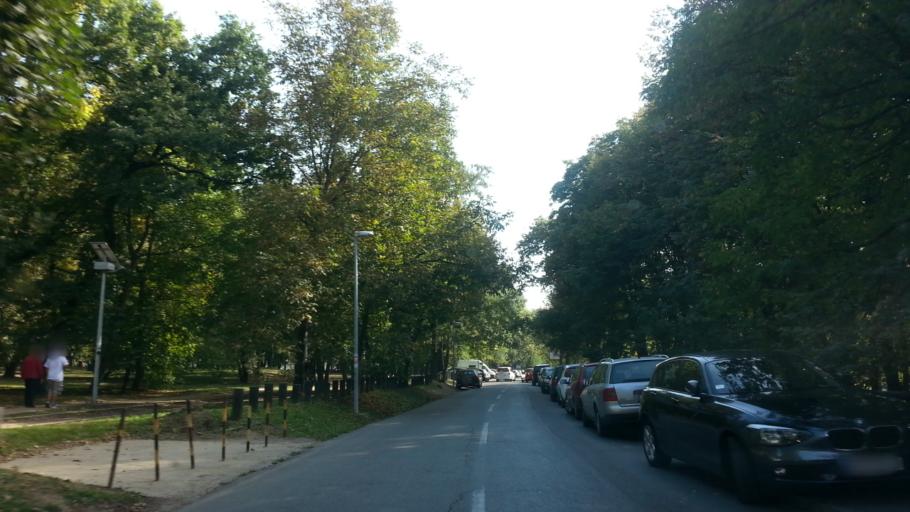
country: RS
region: Central Serbia
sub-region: Belgrade
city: Cukarica
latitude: 44.7675
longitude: 20.4286
